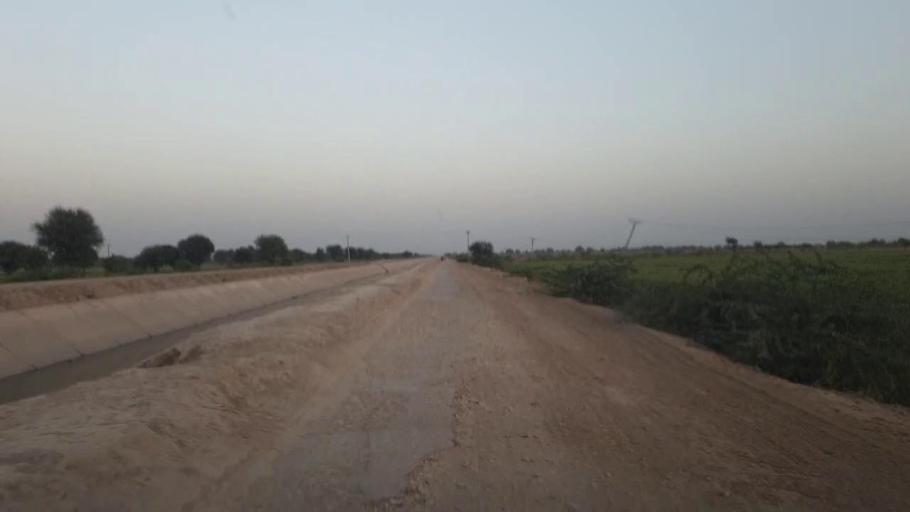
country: PK
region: Sindh
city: Umarkot
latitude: 25.4236
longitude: 69.6622
